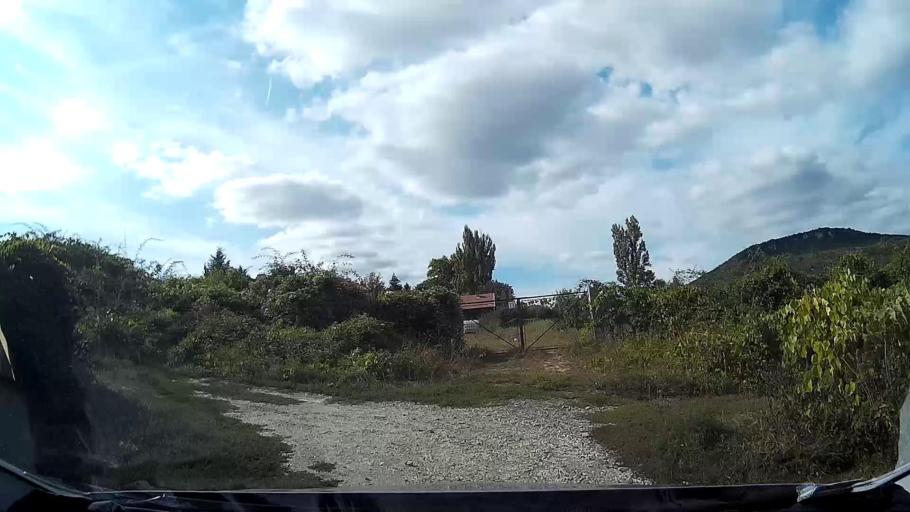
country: HU
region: Pest
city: Nagykovacsi
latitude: 47.6610
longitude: 19.0177
